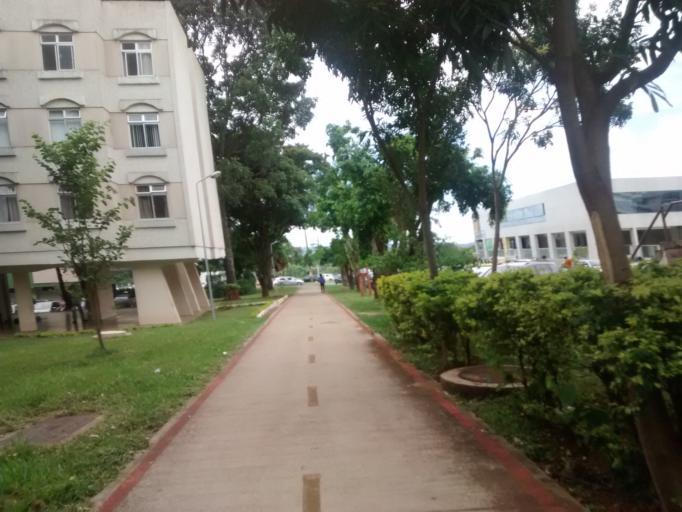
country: BR
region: Federal District
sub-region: Brasilia
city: Brasilia
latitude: -15.7659
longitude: -47.8774
